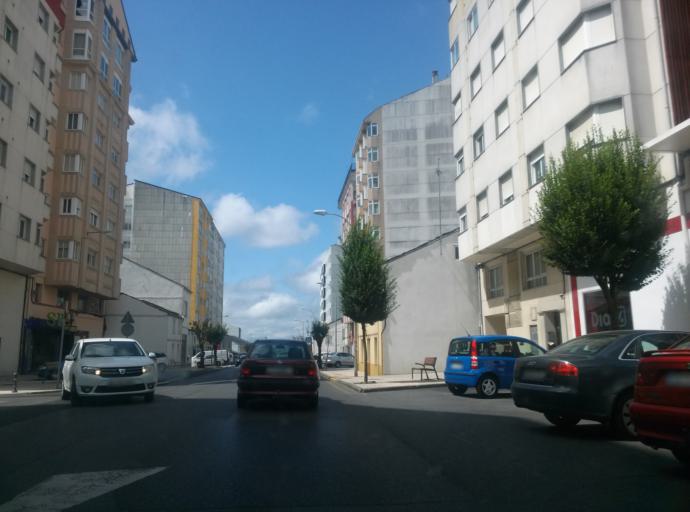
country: ES
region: Galicia
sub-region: Provincia de Lugo
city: Lugo
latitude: 43.0303
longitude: -7.5710
